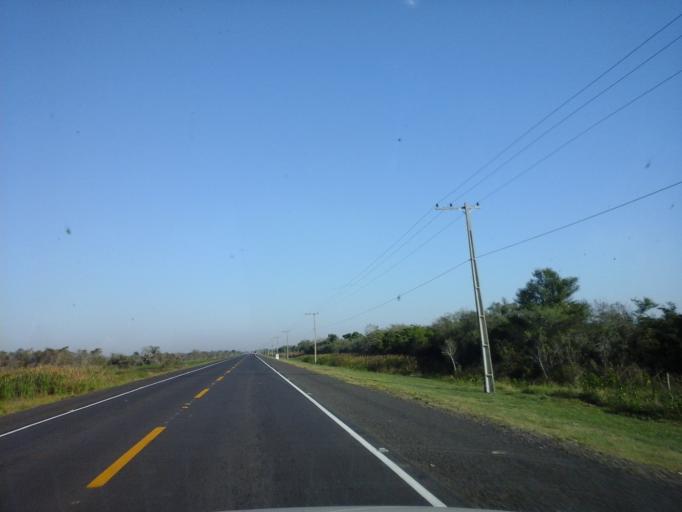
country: PY
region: Neembucu
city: Pilar
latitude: -26.8586
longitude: -58.1811
